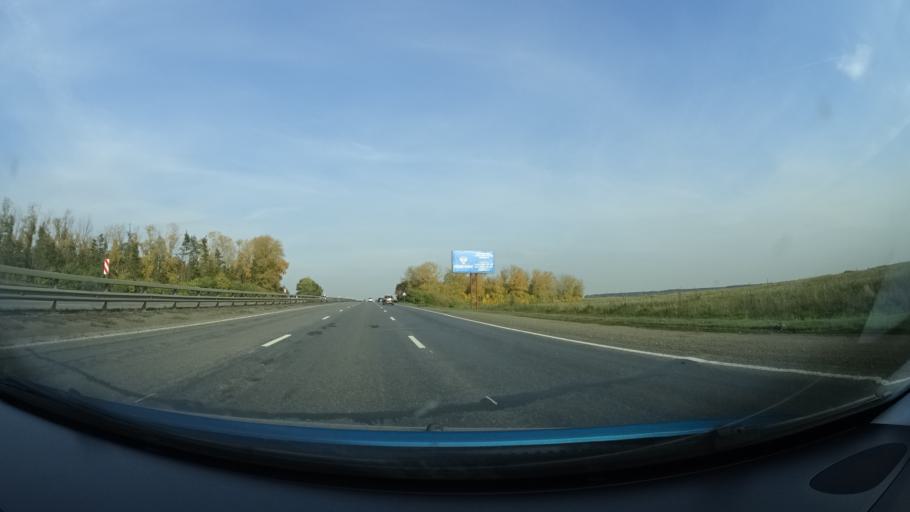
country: RU
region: Bashkortostan
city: Avdon
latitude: 54.6687
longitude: 55.7570
